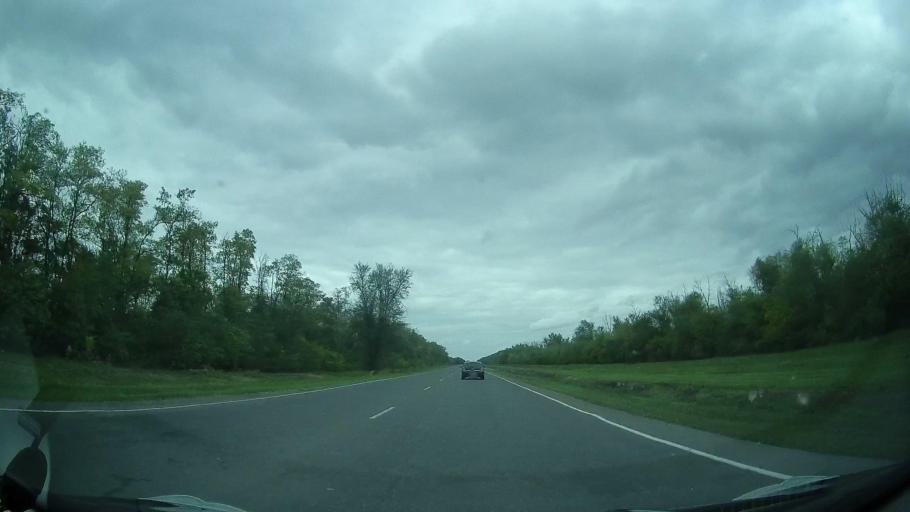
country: RU
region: Rostov
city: Yegorlykskaya
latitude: 46.5952
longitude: 40.6239
